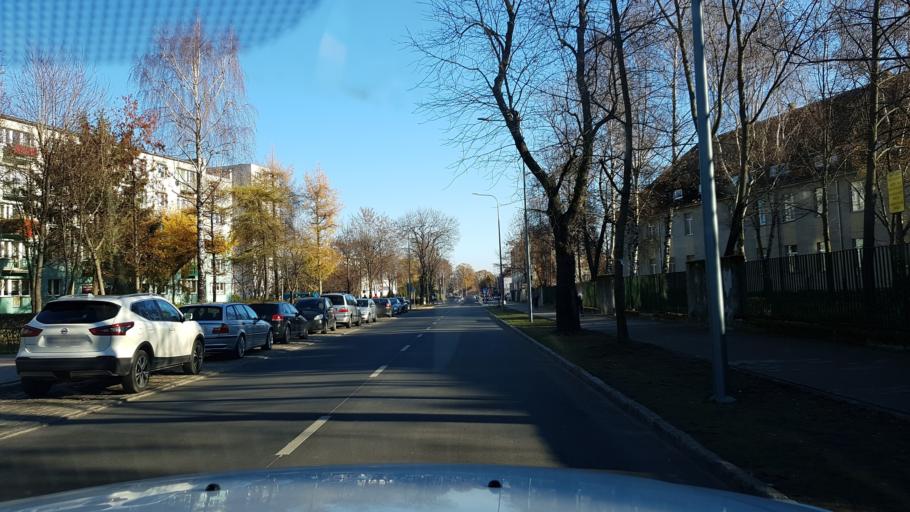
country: PL
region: West Pomeranian Voivodeship
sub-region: Powiat stargardzki
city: Stargard Szczecinski
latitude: 53.3365
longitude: 15.0099
